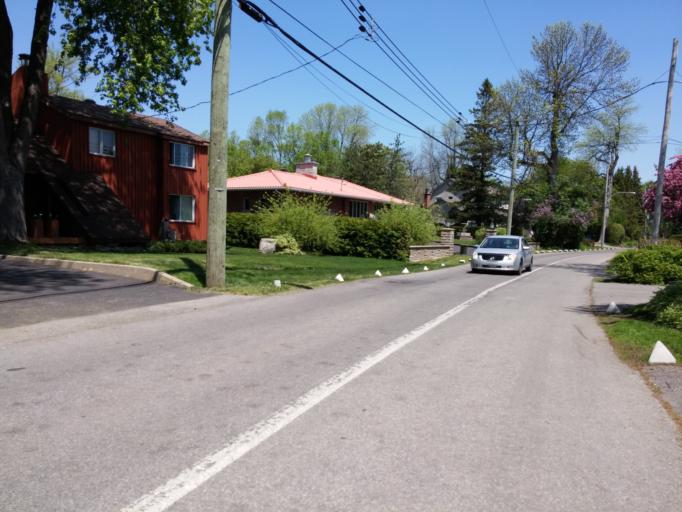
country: CA
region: Quebec
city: Beaconsfield
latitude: 45.4191
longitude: -73.8760
